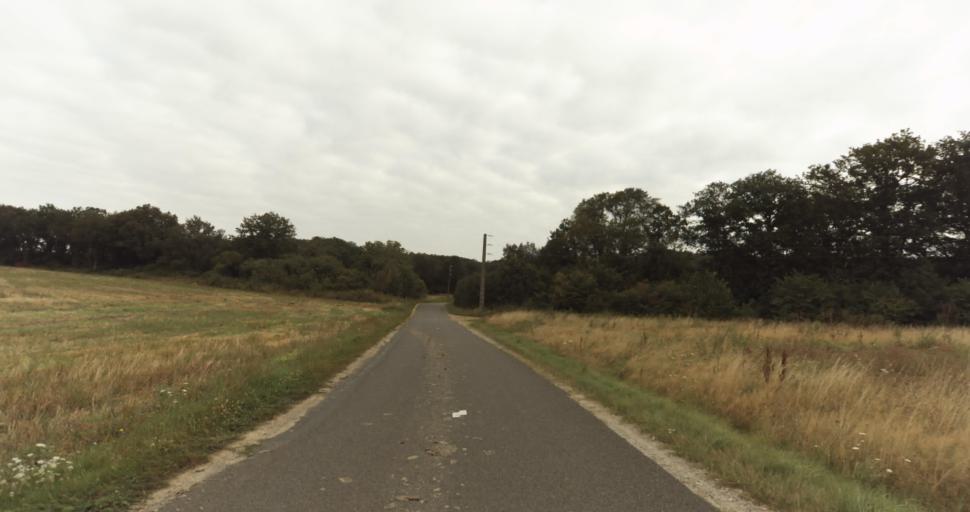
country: FR
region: Haute-Normandie
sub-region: Departement de l'Eure
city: Marcilly-sur-Eure
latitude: 48.8329
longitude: 1.3019
